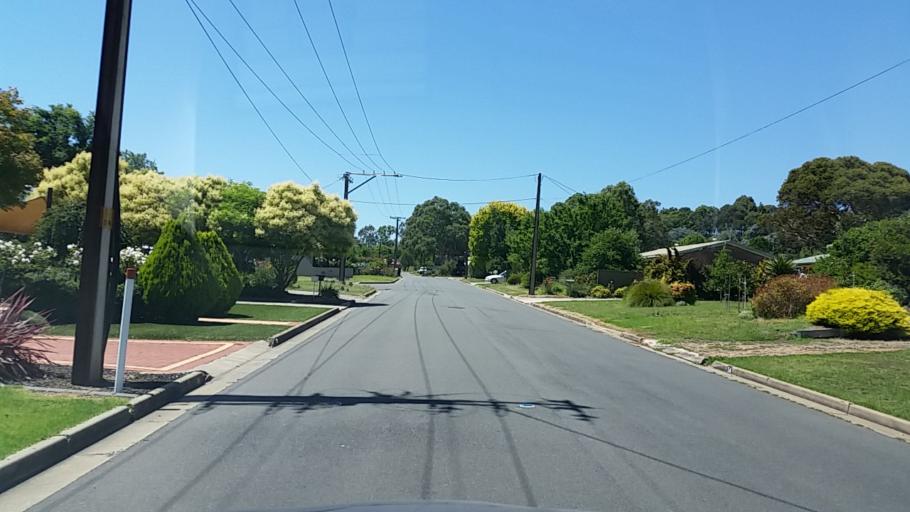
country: AU
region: South Australia
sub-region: Adelaide Hills
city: Balhannah
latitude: -34.9926
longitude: 138.8301
